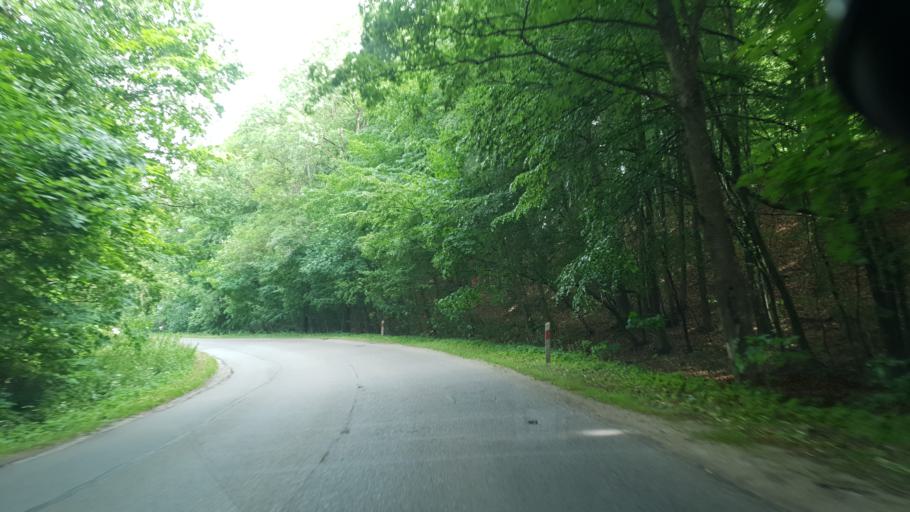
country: PL
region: Pomeranian Voivodeship
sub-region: Powiat kartuski
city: Przodkowo
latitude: 54.3584
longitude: 18.2530
